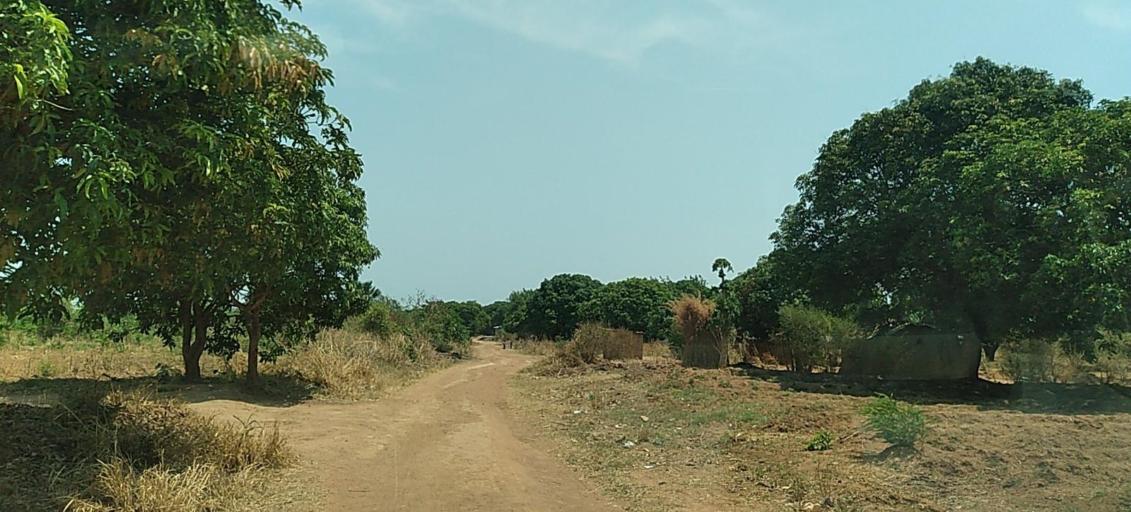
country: ZM
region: Copperbelt
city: Ndola
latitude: -13.0772
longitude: 28.7470
